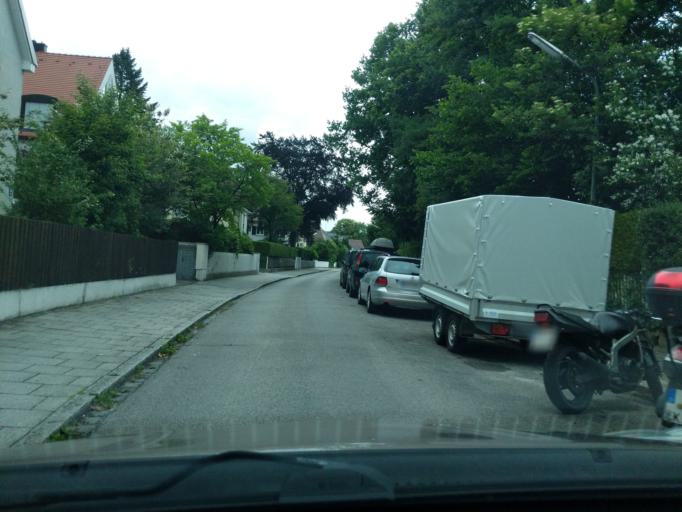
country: DE
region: Bavaria
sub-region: Upper Bavaria
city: Pullach im Isartal
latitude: 48.1107
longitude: 11.5140
